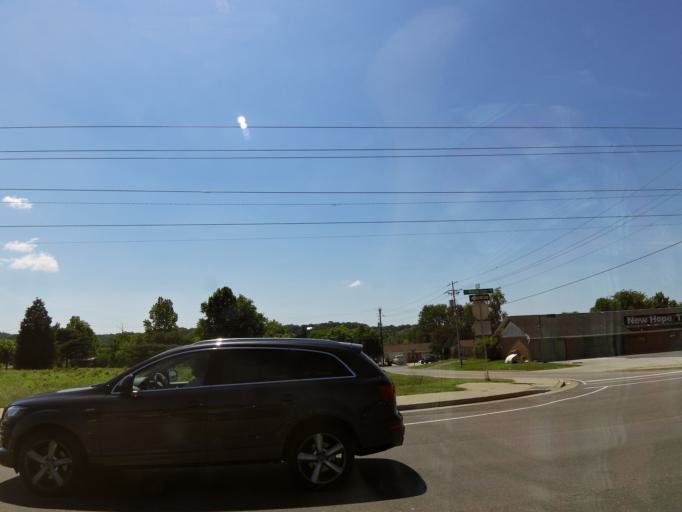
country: US
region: Tennessee
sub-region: Sevier County
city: Sevierville
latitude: 35.9191
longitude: -83.5806
